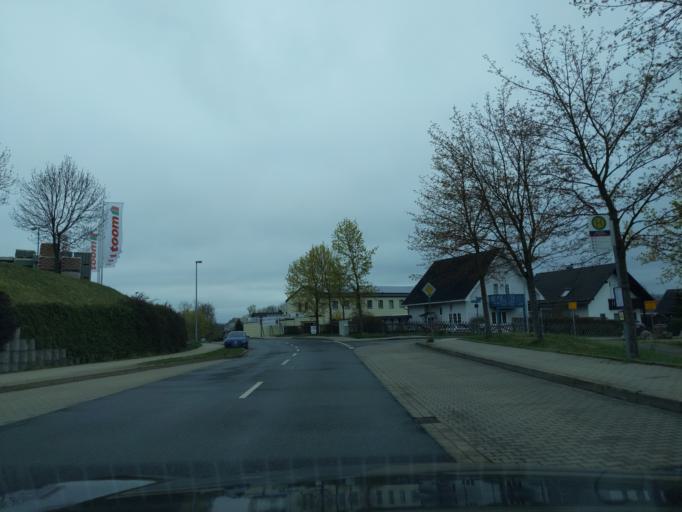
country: DE
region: Saxony
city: Schneeberg
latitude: 50.6035
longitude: 12.6472
